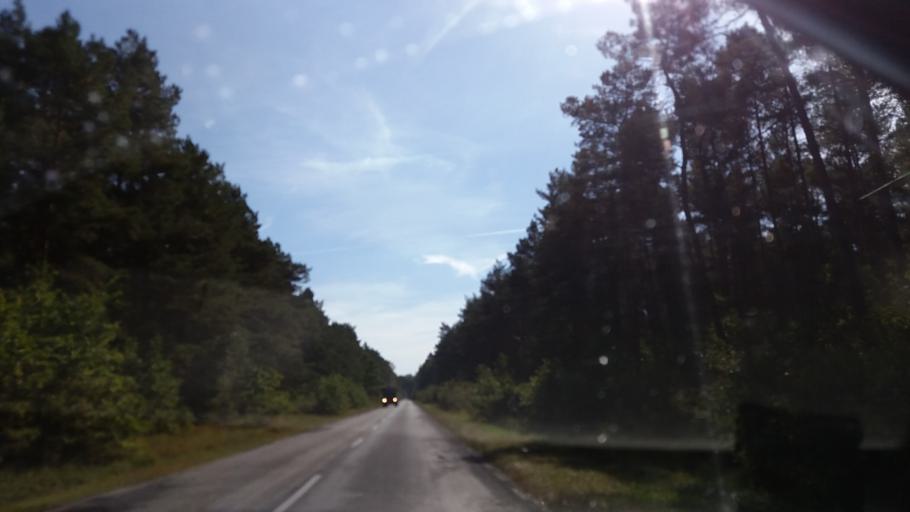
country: PL
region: Lubusz
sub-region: Powiat strzelecko-drezdenecki
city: Drezdenko
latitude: 52.8001
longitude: 15.8327
